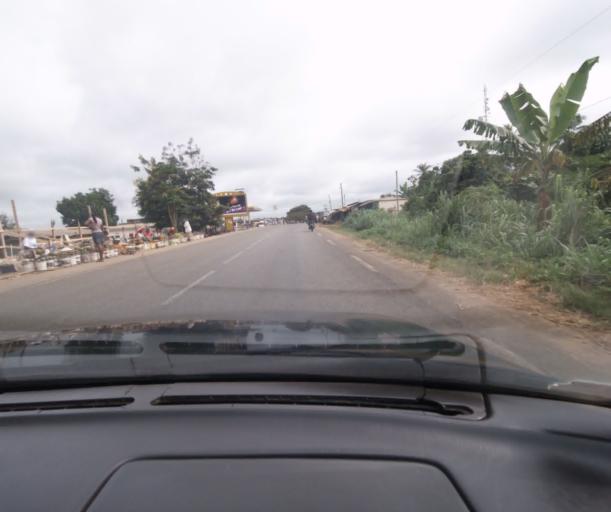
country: CM
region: Centre
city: Ombesa
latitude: 4.6018
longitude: 11.2568
